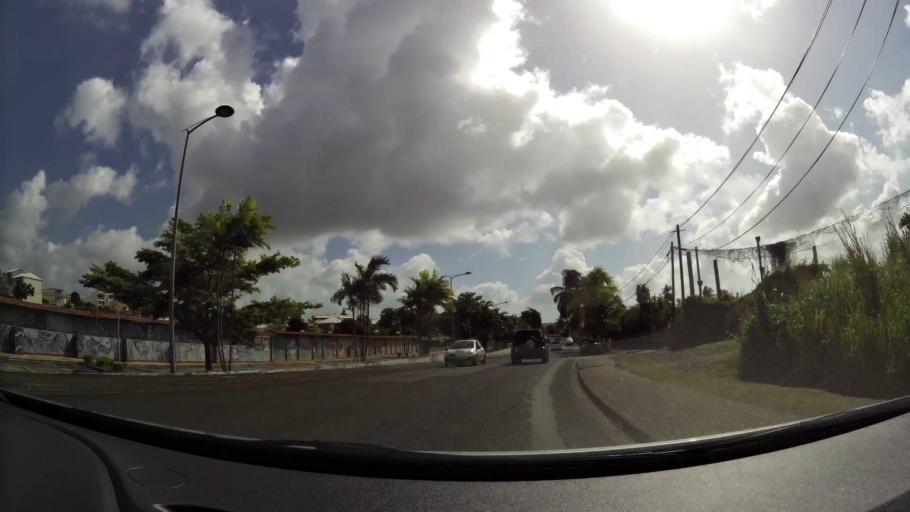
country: MQ
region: Martinique
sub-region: Martinique
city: Le Lamentin
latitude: 14.6151
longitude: -61.0046
